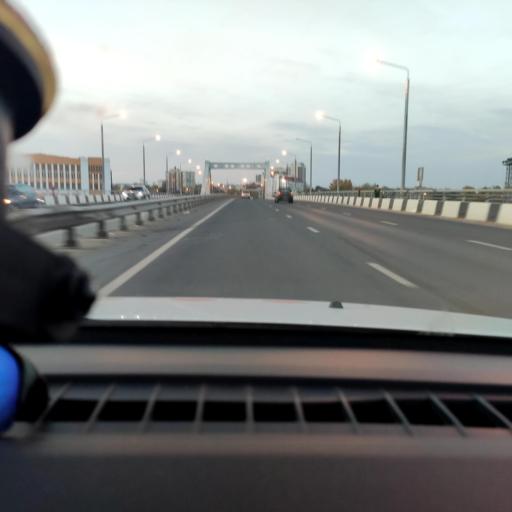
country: RU
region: Samara
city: Rozhdestveno
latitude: 53.1744
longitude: 50.0858
